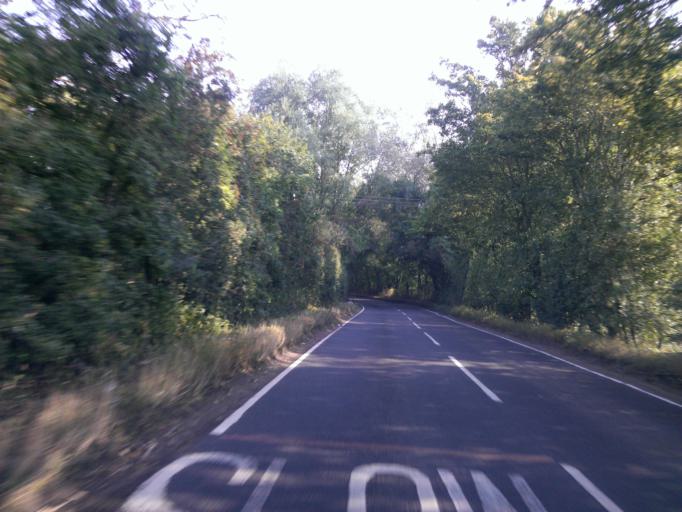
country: GB
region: England
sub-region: Essex
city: Witham
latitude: 51.8137
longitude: 0.6694
